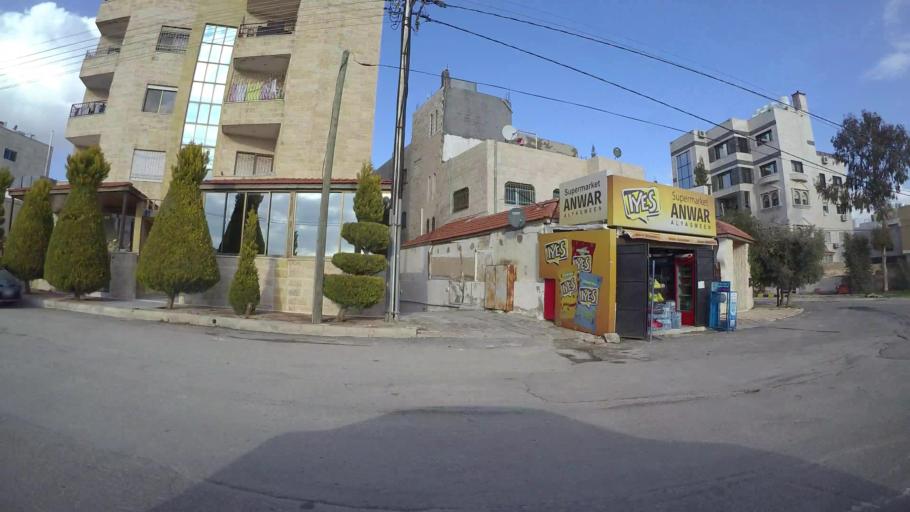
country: JO
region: Amman
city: Al Bunayyat ash Shamaliyah
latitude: 31.9081
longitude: 35.8807
